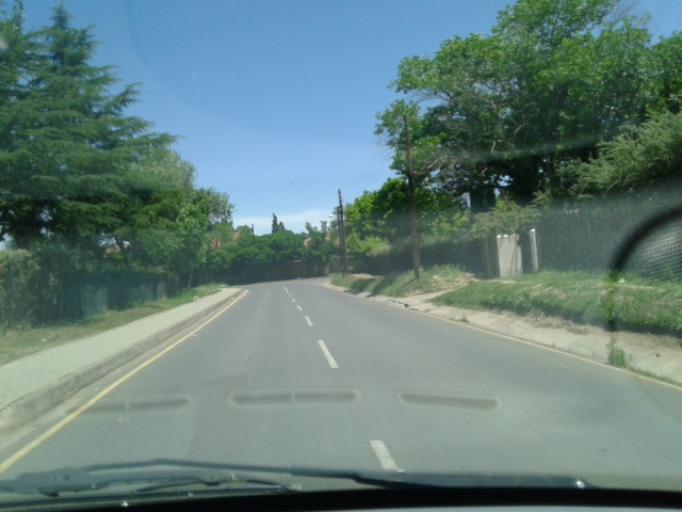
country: LS
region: Maseru
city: Maseru
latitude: -29.3076
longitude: 27.4787
